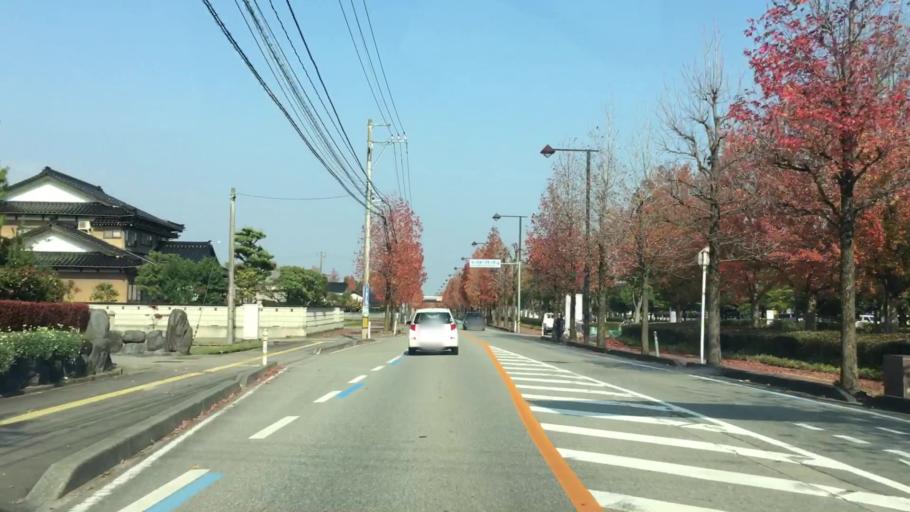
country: JP
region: Toyama
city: Toyama-shi
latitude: 36.6236
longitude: 137.1932
